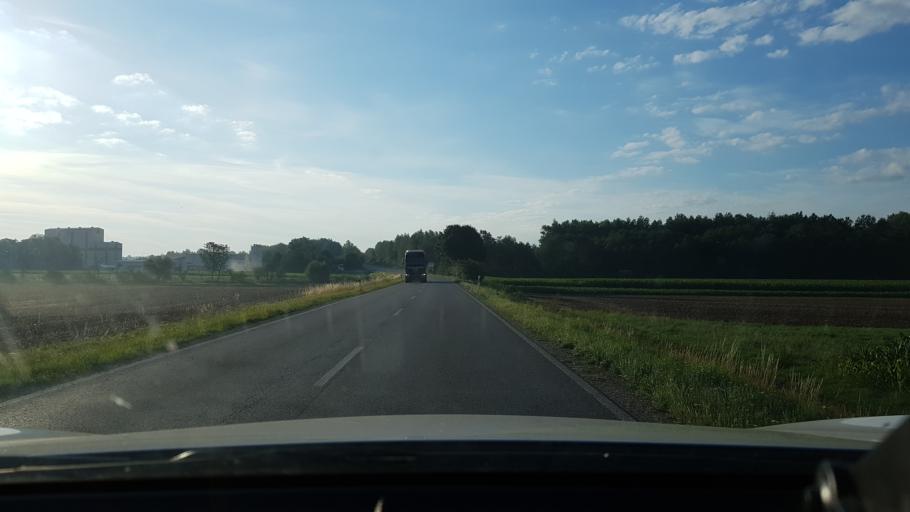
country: DE
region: Baden-Wuerttemberg
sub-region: Tuebingen Region
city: Warthausen
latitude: 48.1577
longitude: 9.8305
